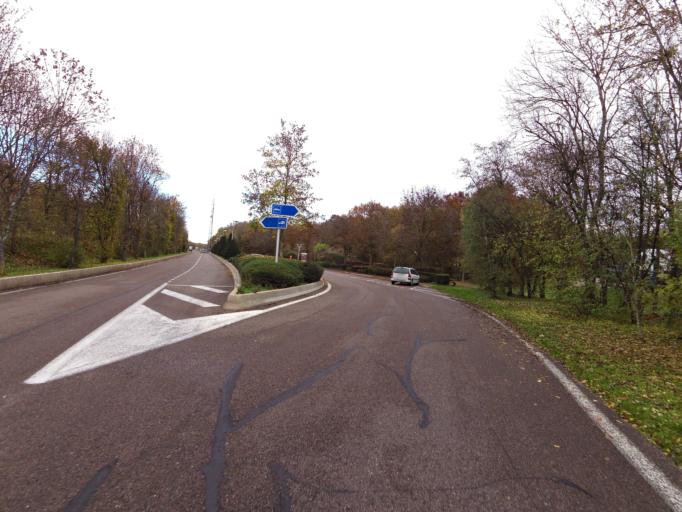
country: FR
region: Bourgogne
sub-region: Departement de Saone-et-Loire
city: Champforgeuil
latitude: 46.8605
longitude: 4.8234
